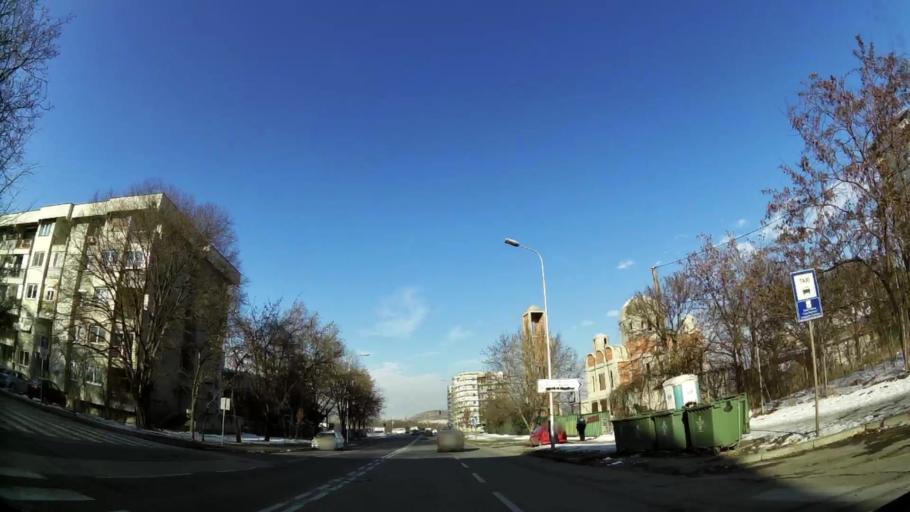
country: MK
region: Karpos
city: Skopje
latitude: 42.0068
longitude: 21.3910
